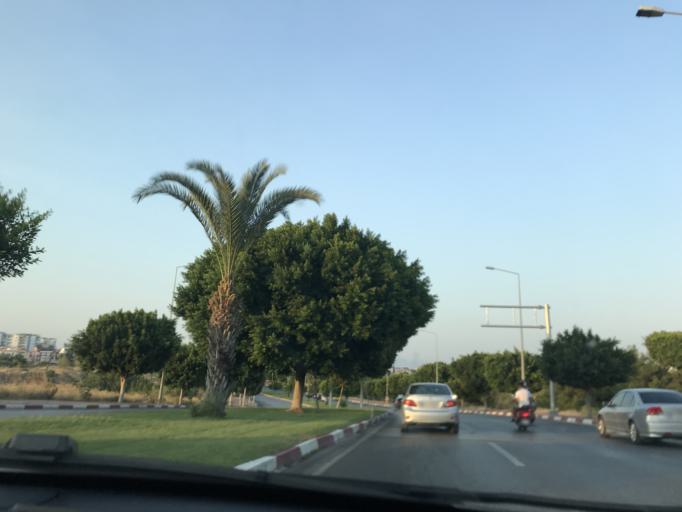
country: TR
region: Antalya
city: Antalya
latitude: 36.8683
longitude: 30.6389
